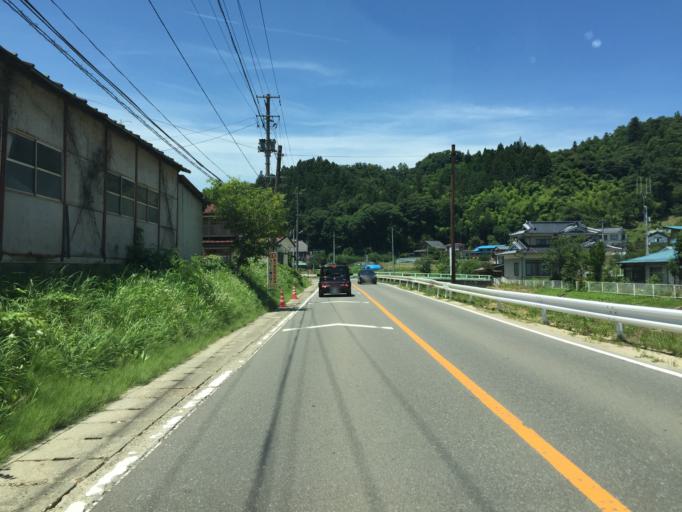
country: JP
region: Fukushima
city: Yanagawamachi-saiwaicho
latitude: 37.7613
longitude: 140.6288
